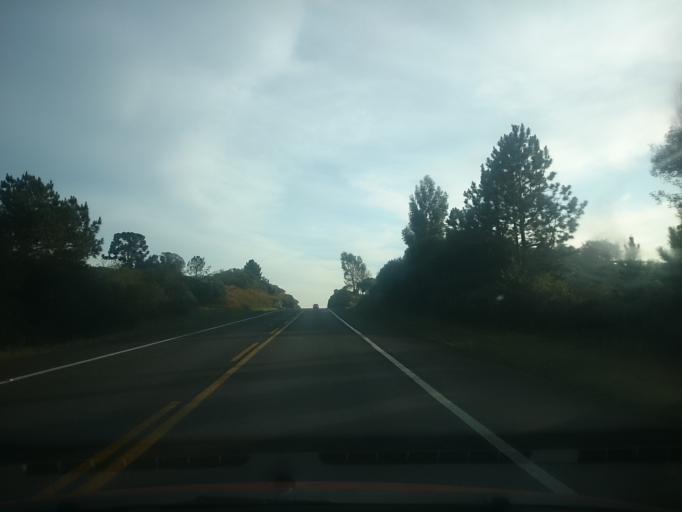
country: BR
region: Rio Grande do Sul
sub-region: Vacaria
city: Vacaria
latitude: -28.3148
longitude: -50.8039
